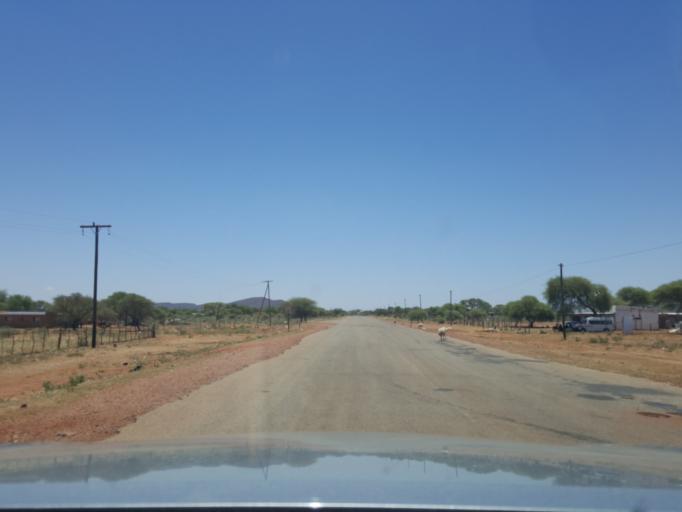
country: BW
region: South East
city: Ramotswa
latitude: -24.9867
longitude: 25.8971
